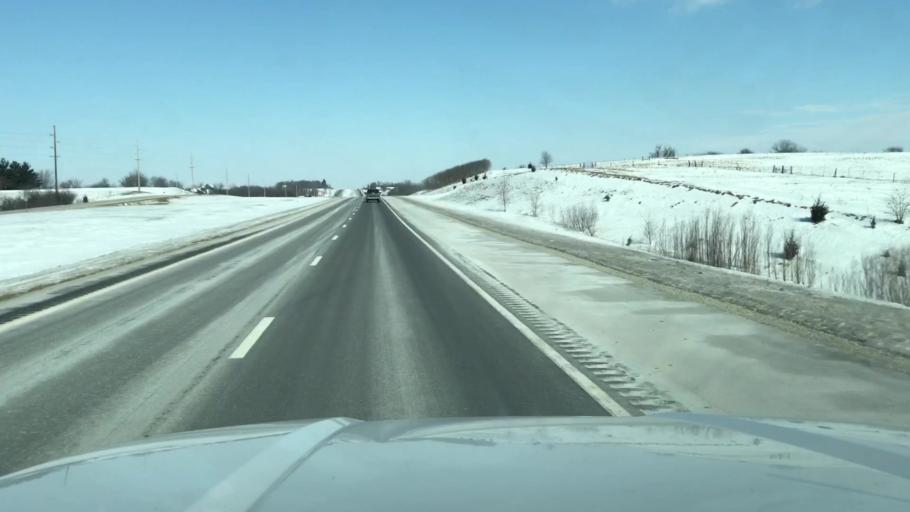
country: US
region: Missouri
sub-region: Nodaway County
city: Maryville
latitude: 40.1895
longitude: -94.8678
